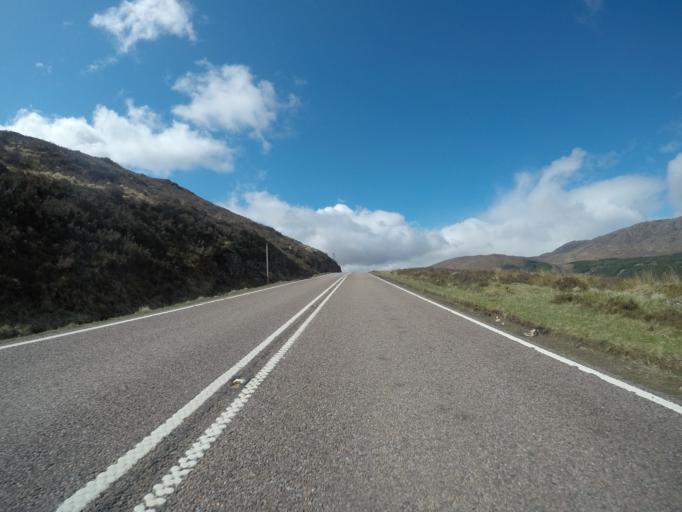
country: GB
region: Scotland
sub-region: Highland
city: Spean Bridge
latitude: 57.1207
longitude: -4.9750
